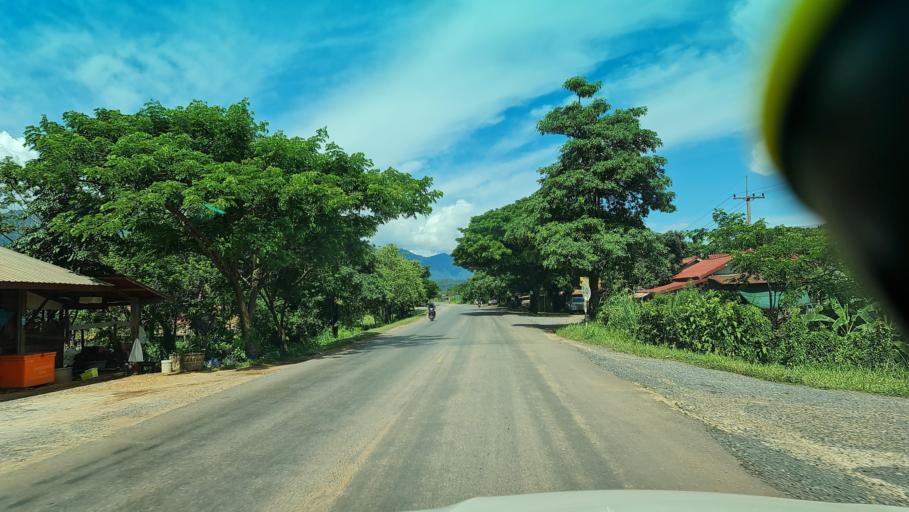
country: LA
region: Bolikhamxai
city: Ban Nahin
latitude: 18.3007
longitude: 104.1149
